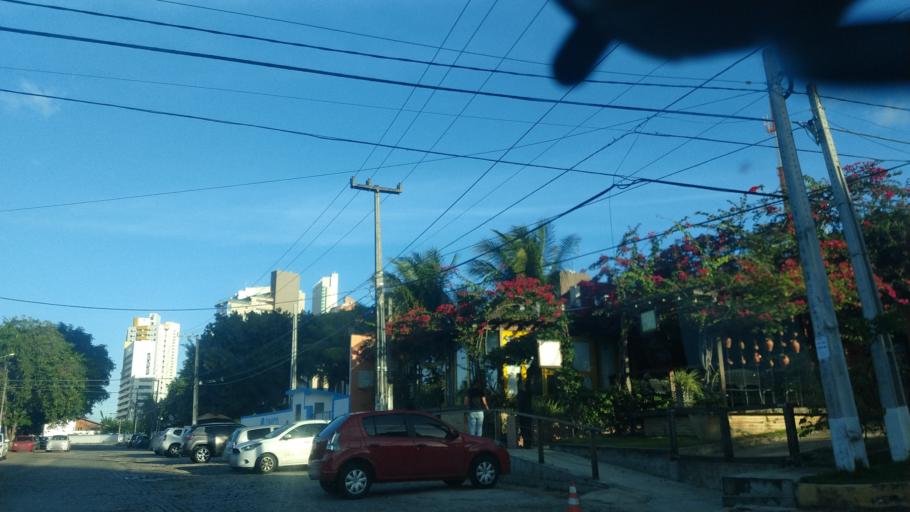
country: BR
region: Rio Grande do Norte
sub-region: Parnamirim
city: Parnamirim
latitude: -5.8809
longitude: -35.1829
